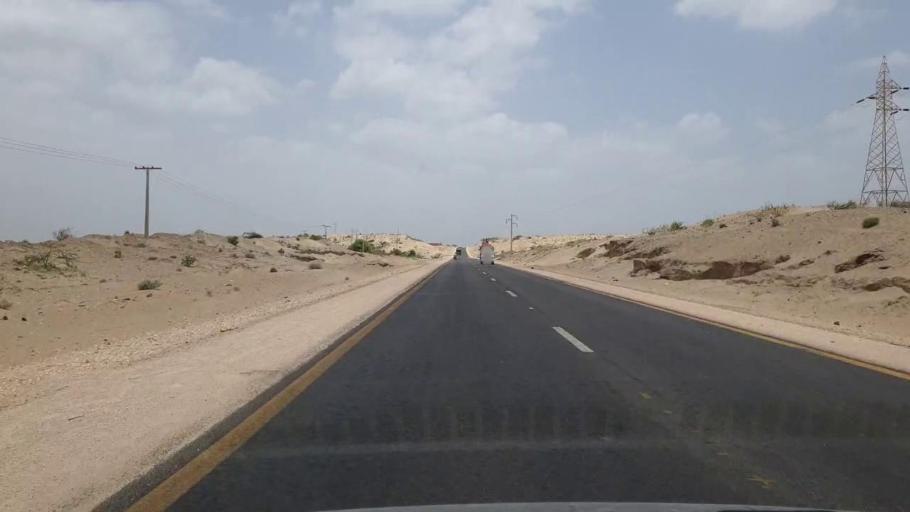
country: PK
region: Sindh
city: Naukot
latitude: 24.8377
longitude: 69.4649
